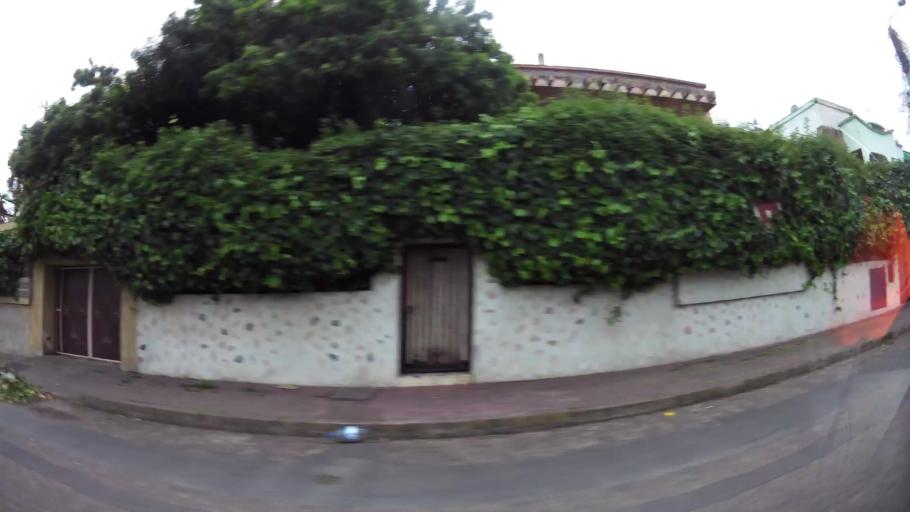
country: MA
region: Grand Casablanca
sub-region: Casablanca
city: Casablanca
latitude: 33.5654
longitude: -7.6172
